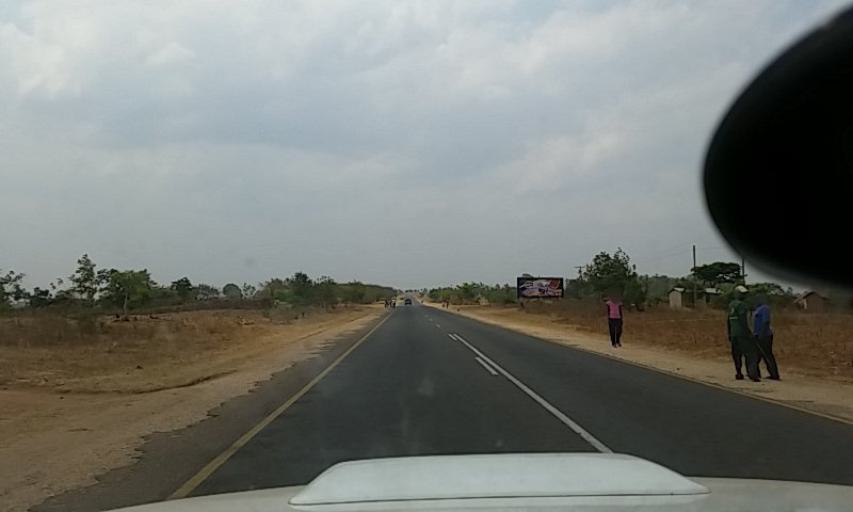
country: MW
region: Central Region
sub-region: Lilongwe District
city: Lilongwe
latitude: -13.8350
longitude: 33.8528
